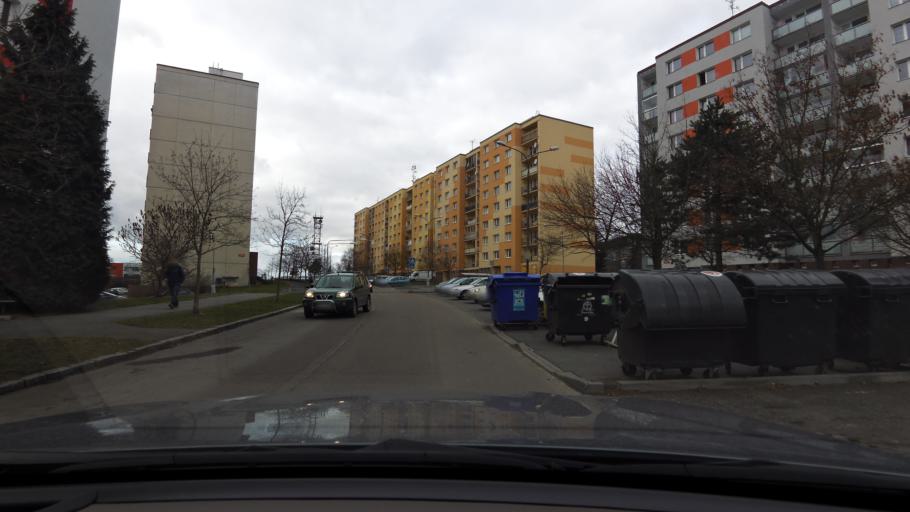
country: CZ
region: Plzensky
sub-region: Okres Plzen-Mesto
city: Pilsen
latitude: 49.7778
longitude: 13.3575
